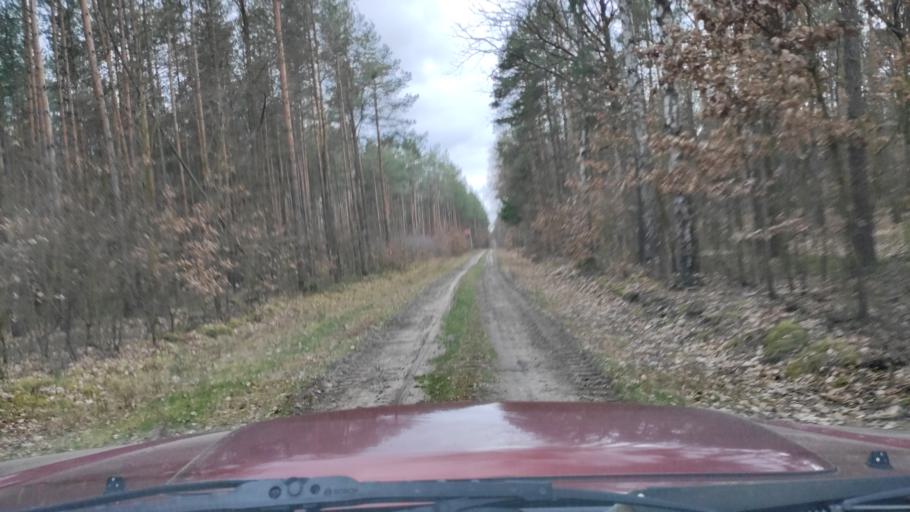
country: PL
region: Masovian Voivodeship
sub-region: Powiat kozienicki
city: Garbatka-Letnisko
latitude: 51.5078
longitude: 21.5516
